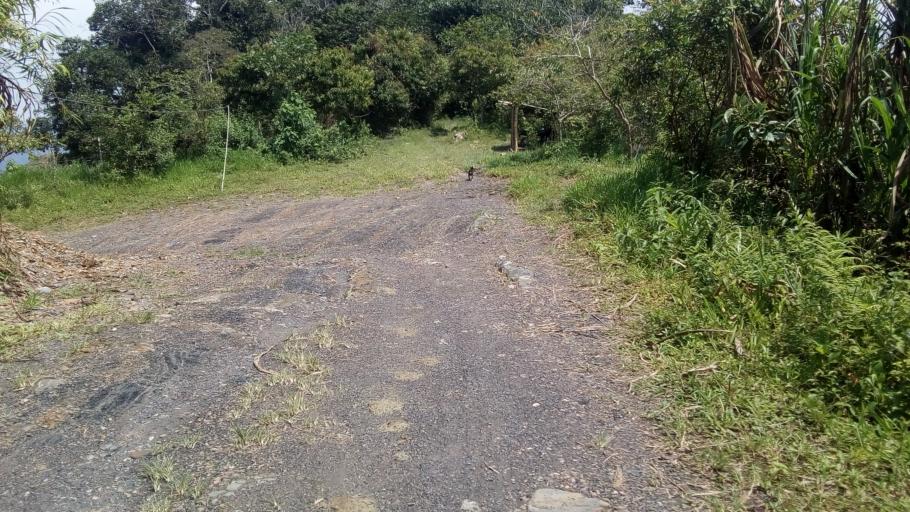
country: CO
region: Boyaca
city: Otanche
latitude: 5.6295
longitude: -74.2421
